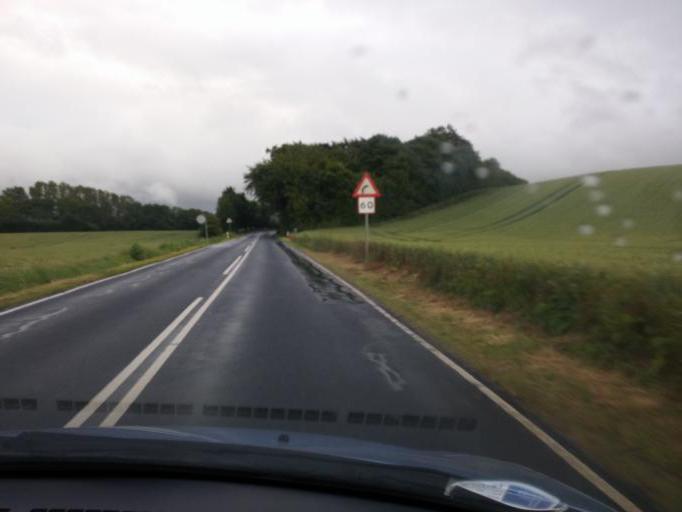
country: DK
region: South Denmark
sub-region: Kerteminde Kommune
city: Kerteminde
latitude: 55.5102
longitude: 10.6514
